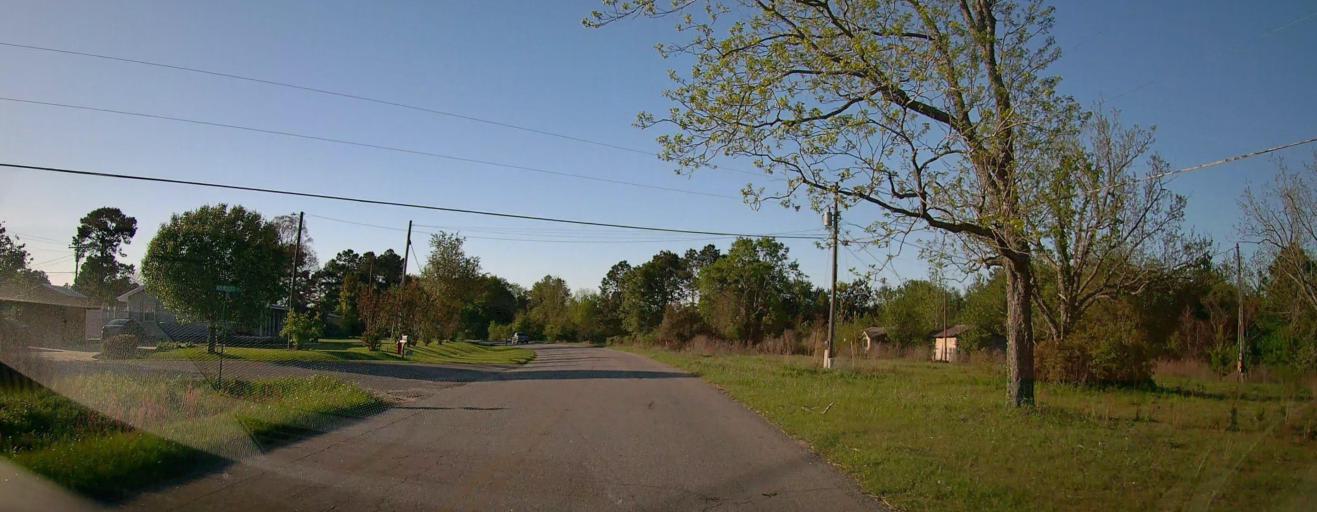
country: US
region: Georgia
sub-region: Ben Hill County
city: Fitzgerald
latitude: 31.6993
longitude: -83.2224
